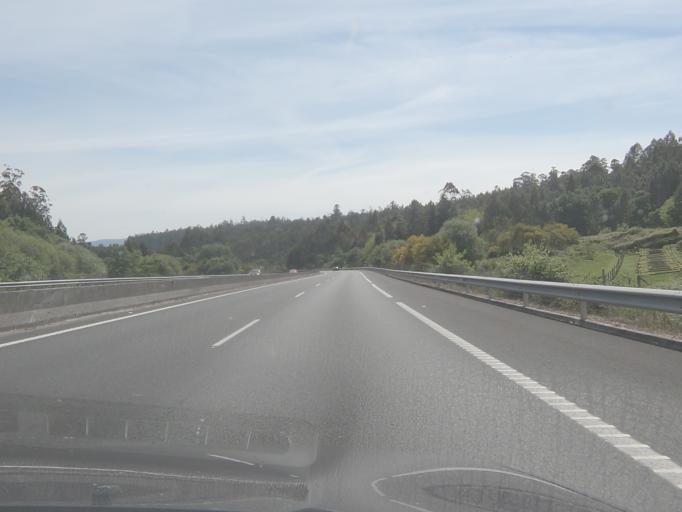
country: ES
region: Galicia
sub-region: Provincia de Pontevedra
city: Caldas de Reis
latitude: 42.6321
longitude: -8.6591
